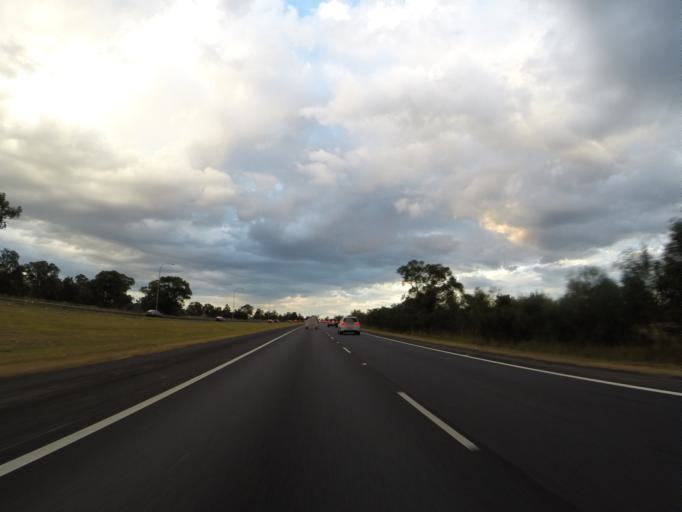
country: AU
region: New South Wales
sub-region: Wollondilly
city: Douglas Park
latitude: -34.2279
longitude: 150.6689
